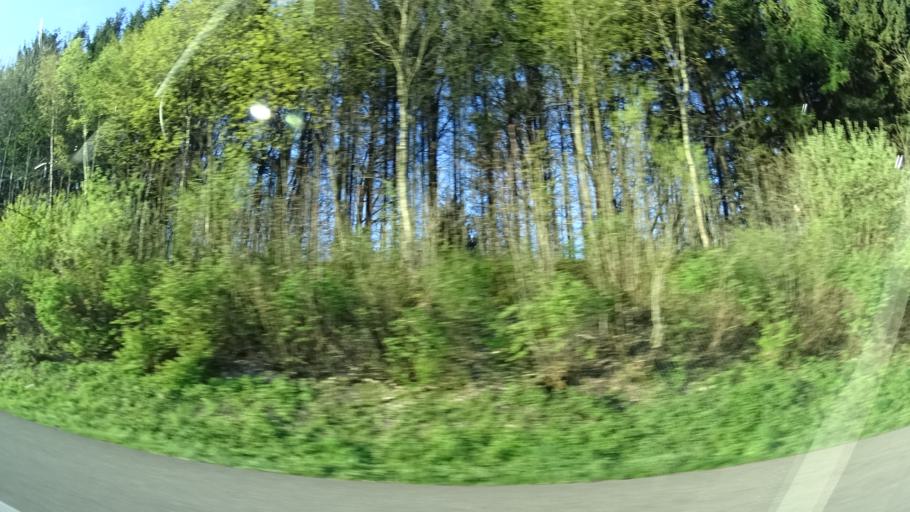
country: DE
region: Baden-Wuerttemberg
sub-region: Regierungsbezirk Stuttgart
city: Untermunkheim
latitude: 49.1823
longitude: 9.7479
